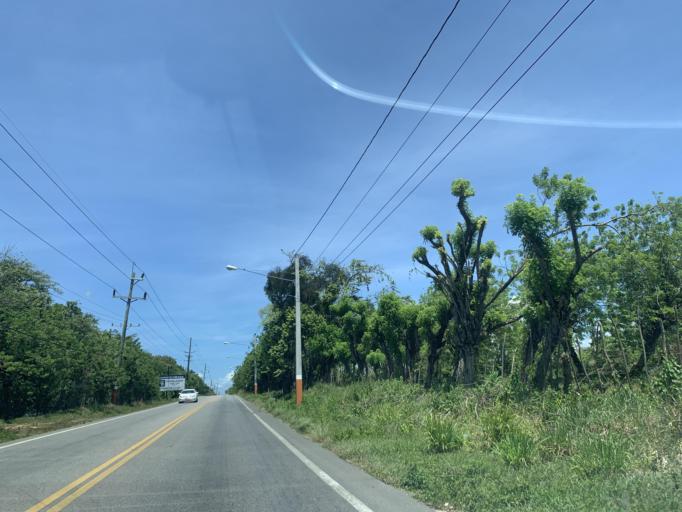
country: DO
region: Puerto Plata
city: Cabarete
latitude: 19.7782
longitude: -70.4756
